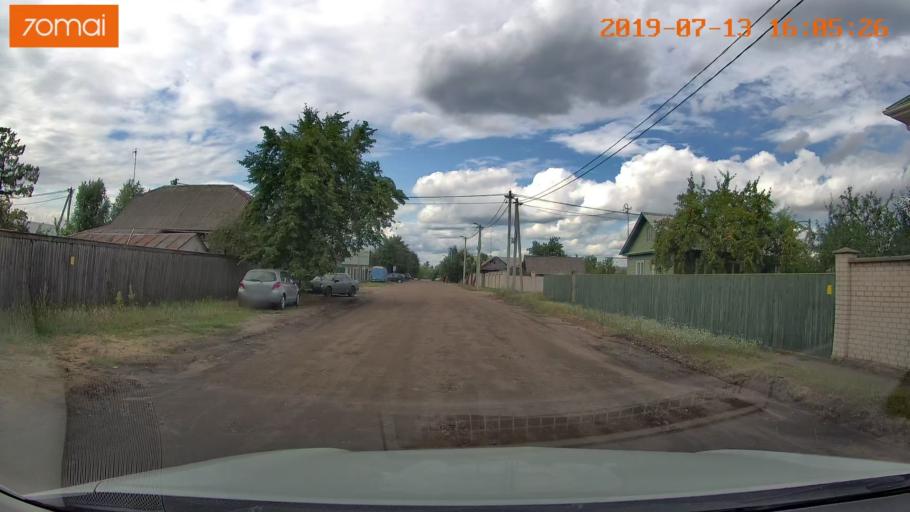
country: BY
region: Mogilev
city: Babruysk
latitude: 53.1487
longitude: 29.2052
